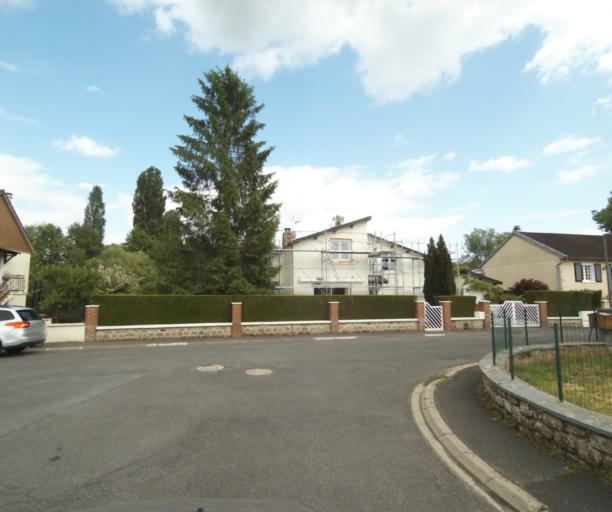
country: FR
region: Champagne-Ardenne
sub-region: Departement des Ardennes
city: Montcy-Notre-Dame
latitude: 49.7580
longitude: 4.7346
